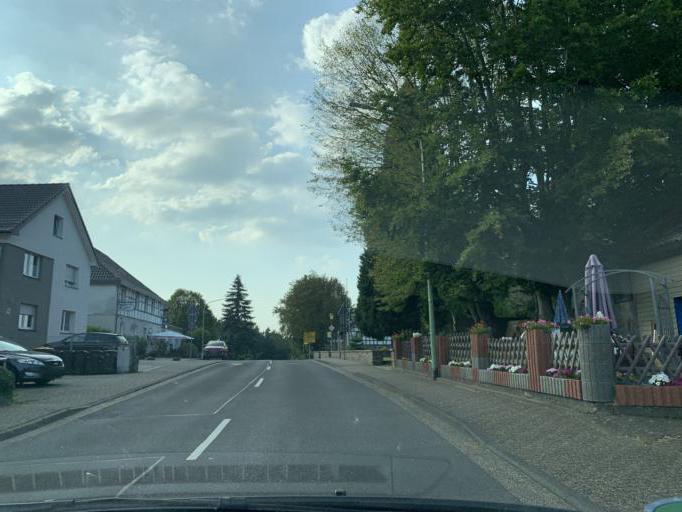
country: DE
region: North Rhine-Westphalia
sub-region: Regierungsbezirk Koln
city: Simmerath
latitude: 50.6271
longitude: 6.3535
